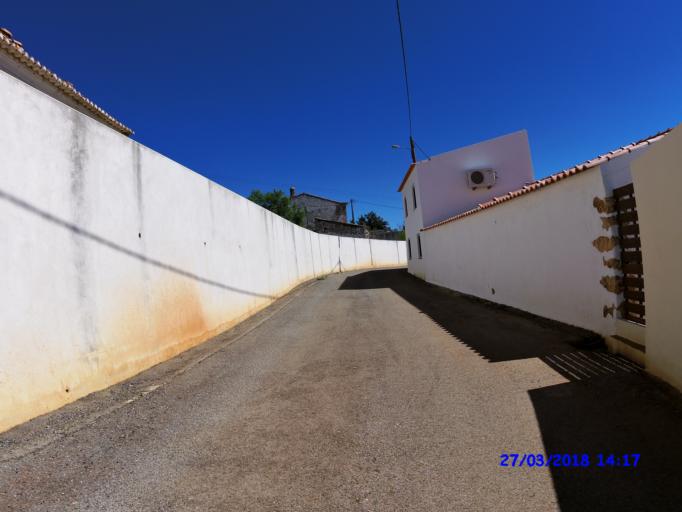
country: PT
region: Faro
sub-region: Loule
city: Boliqueime
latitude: 37.2080
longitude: -8.1684
